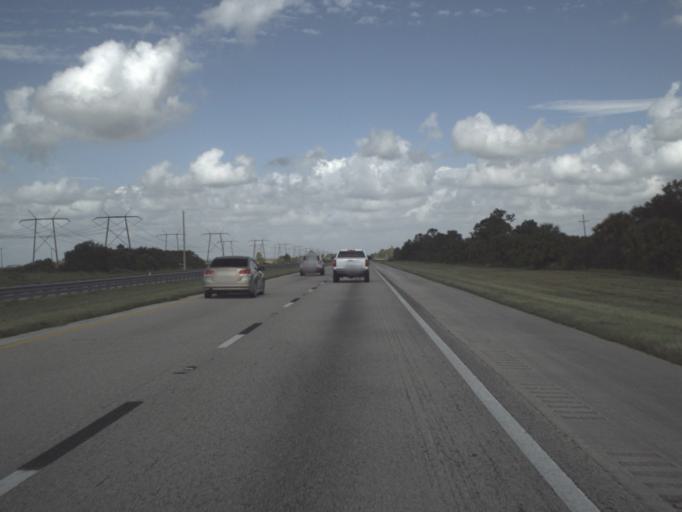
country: US
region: Florida
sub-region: Indian River County
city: West Vero Corridor
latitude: 27.4959
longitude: -80.5765
